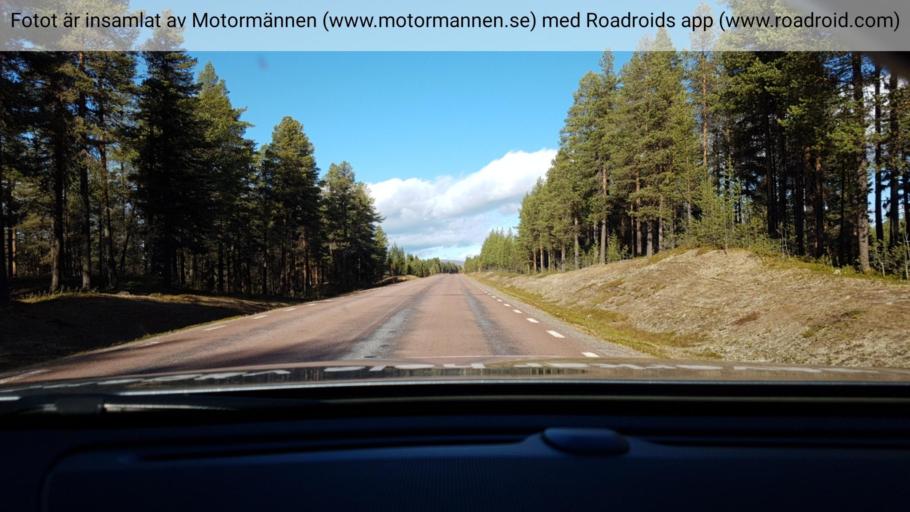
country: SE
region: Norrbotten
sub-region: Arjeplogs Kommun
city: Arjeplog
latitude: 66.0215
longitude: 18.0713
